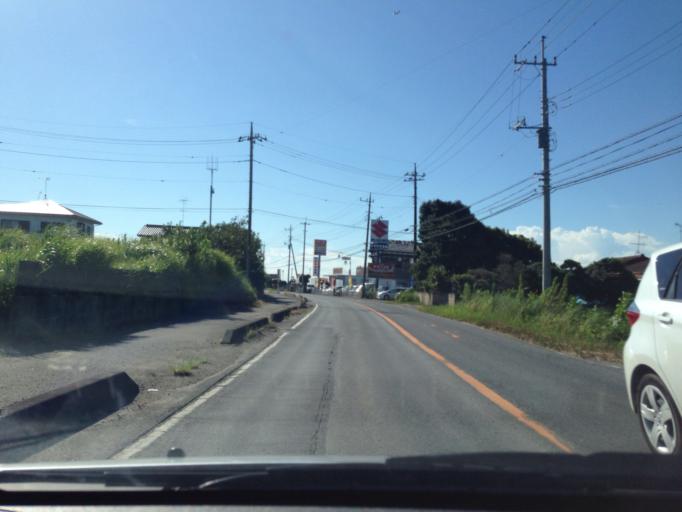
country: JP
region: Ibaraki
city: Inashiki
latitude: 36.0257
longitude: 140.2881
